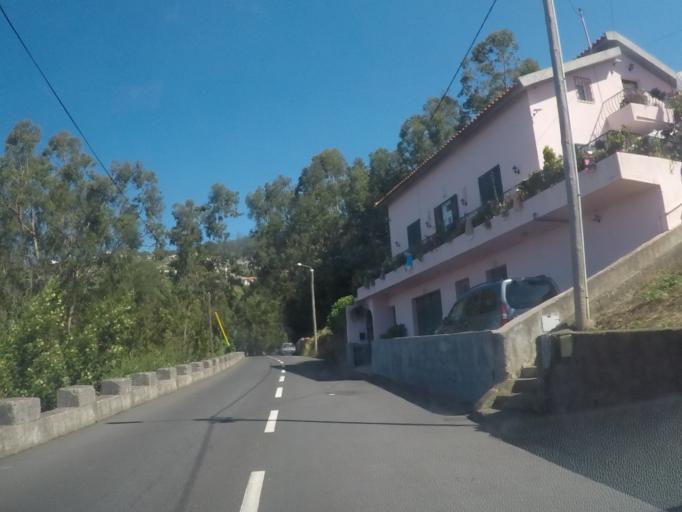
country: PT
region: Madeira
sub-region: Camara de Lobos
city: Curral das Freiras
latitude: 32.6787
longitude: -16.9667
